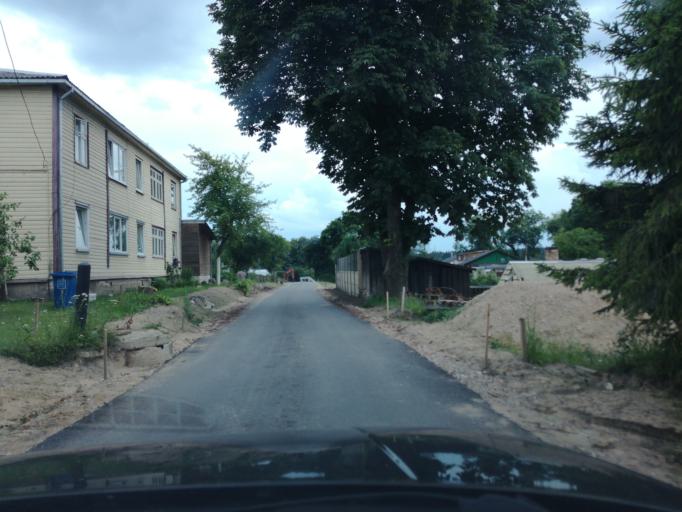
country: LT
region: Alytaus apskritis
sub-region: Alytus
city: Alytus
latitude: 54.4004
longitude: 24.0704
